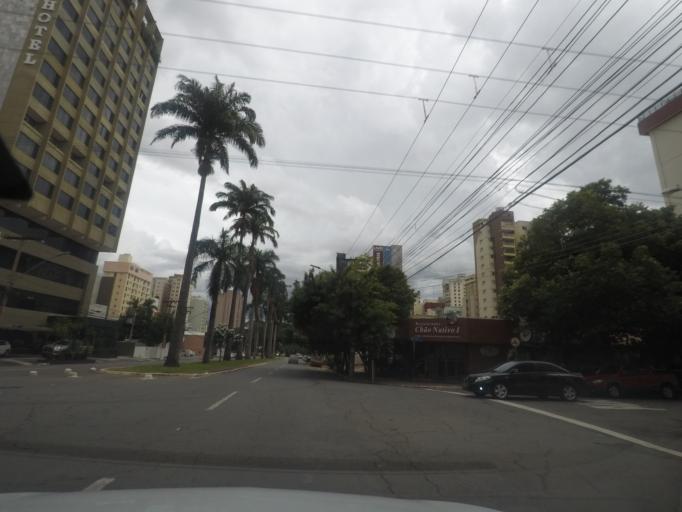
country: BR
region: Goias
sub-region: Goiania
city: Goiania
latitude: -16.6821
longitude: -49.2662
